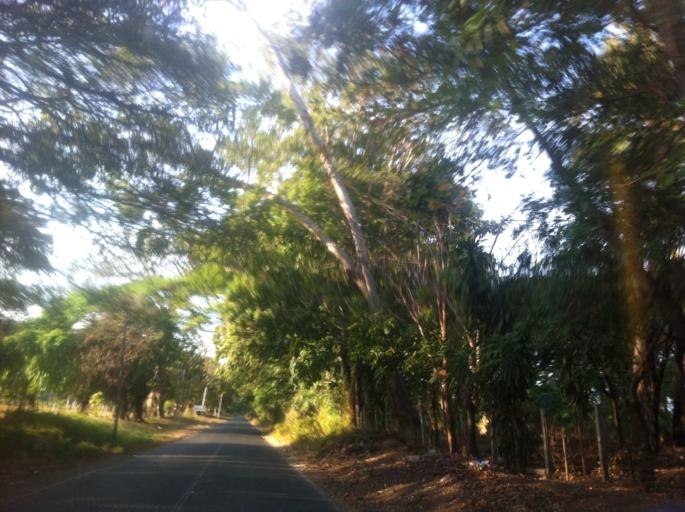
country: NI
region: Rivas
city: Rivas
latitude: 11.4573
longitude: -85.8421
